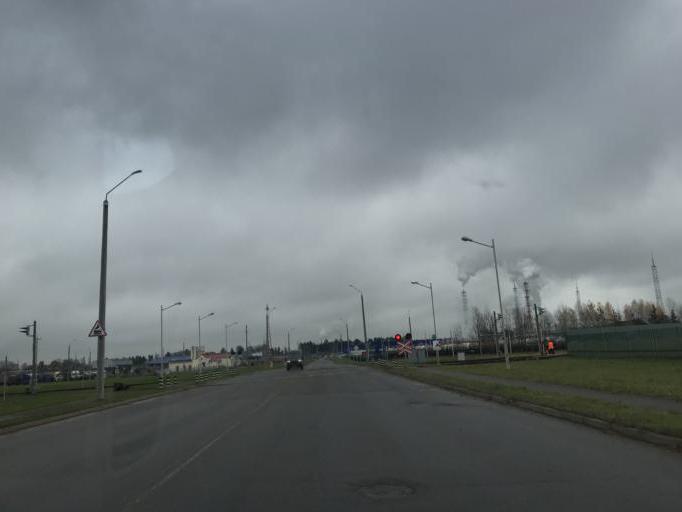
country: BY
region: Mogilev
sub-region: Mahilyowski Rayon
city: Veyno
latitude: 53.8288
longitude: 30.3457
